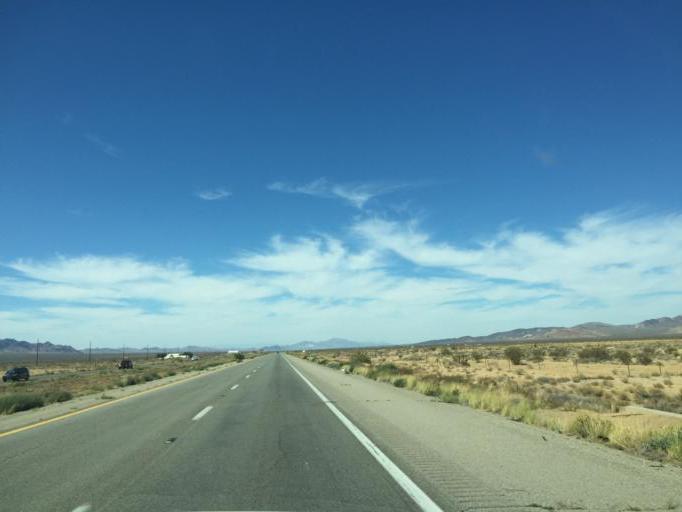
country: US
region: Arizona
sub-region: Mohave County
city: Dolan Springs
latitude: 35.5436
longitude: -114.3619
